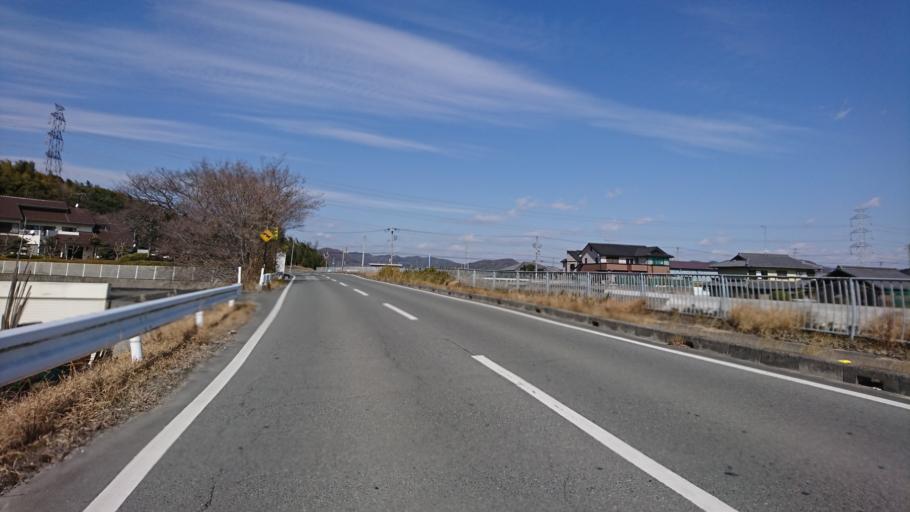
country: JP
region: Hyogo
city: Kakogawacho-honmachi
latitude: 34.7983
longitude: 134.8114
